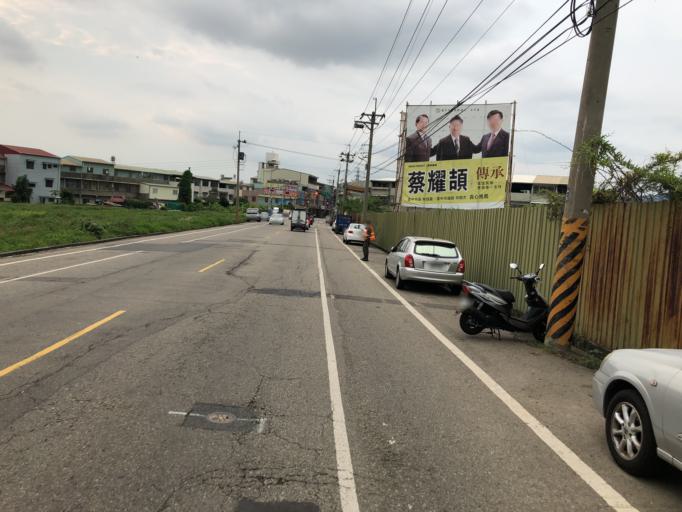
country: TW
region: Taiwan
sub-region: Taichung City
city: Taichung
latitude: 24.0947
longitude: 120.7291
